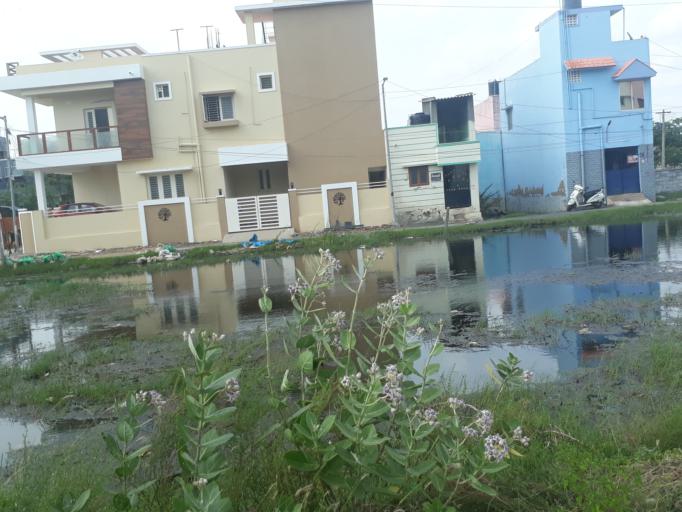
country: IN
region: Tamil Nadu
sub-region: Kancheepuram
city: Perungudi
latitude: 12.9524
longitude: 80.2337
